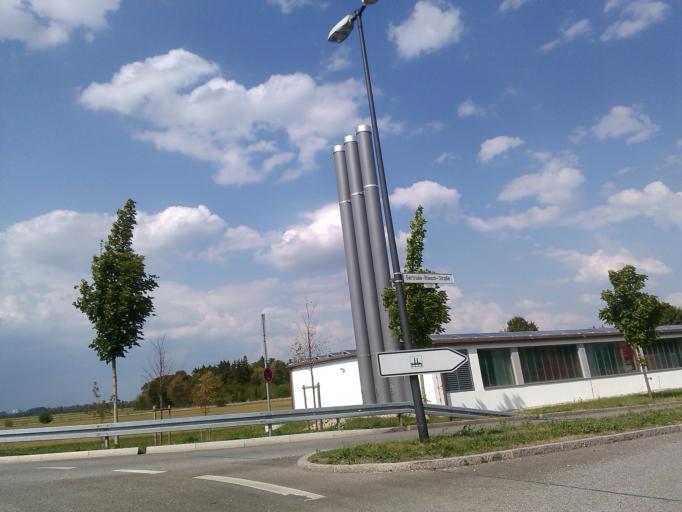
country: DE
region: Bavaria
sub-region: Upper Bavaria
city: Germering
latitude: 48.1411
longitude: 11.3709
